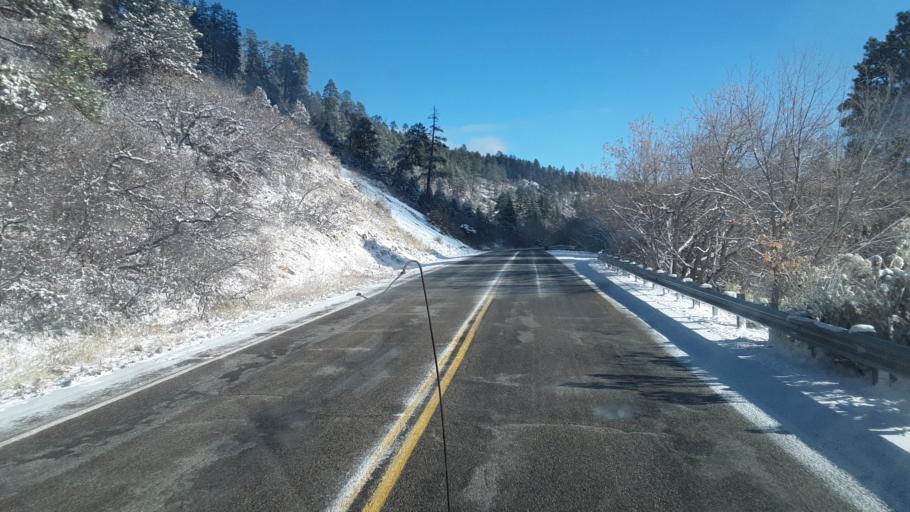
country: US
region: Colorado
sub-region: La Plata County
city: Durango
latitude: 37.3234
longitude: -107.7640
